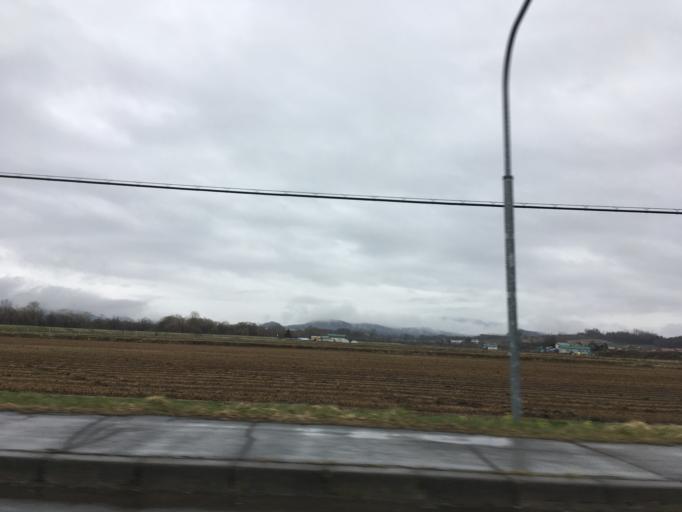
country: JP
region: Hokkaido
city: Nayoro
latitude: 44.1252
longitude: 142.4836
